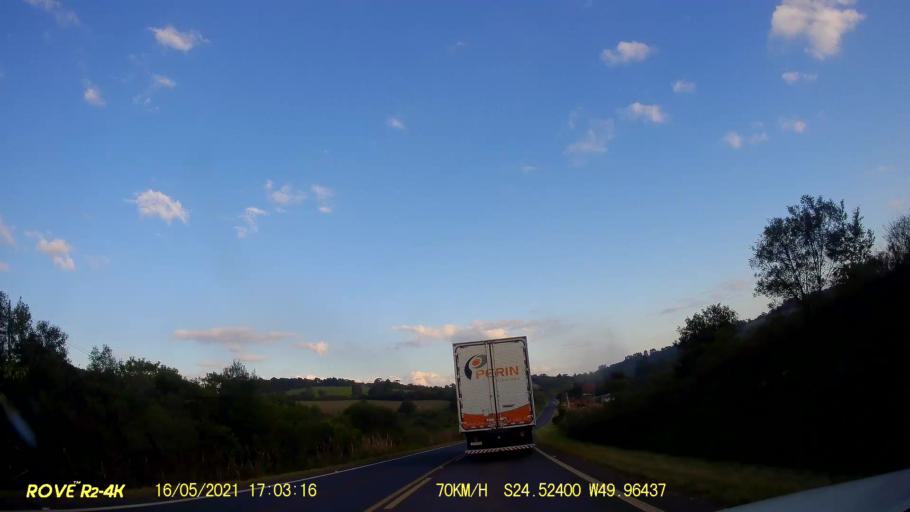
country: BR
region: Parana
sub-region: Pirai Do Sul
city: Pirai do Sul
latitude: -24.5241
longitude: -49.9648
